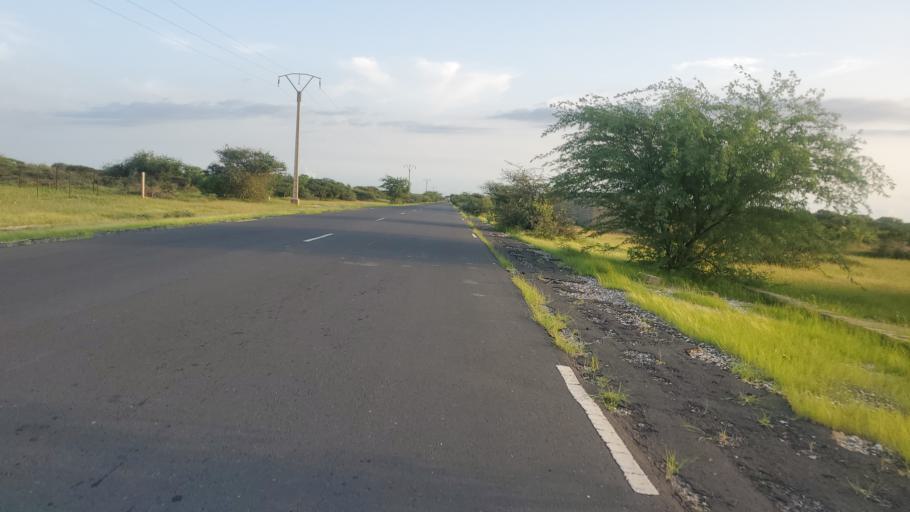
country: SN
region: Saint-Louis
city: Saint-Louis
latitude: 16.1763
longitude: -16.4097
